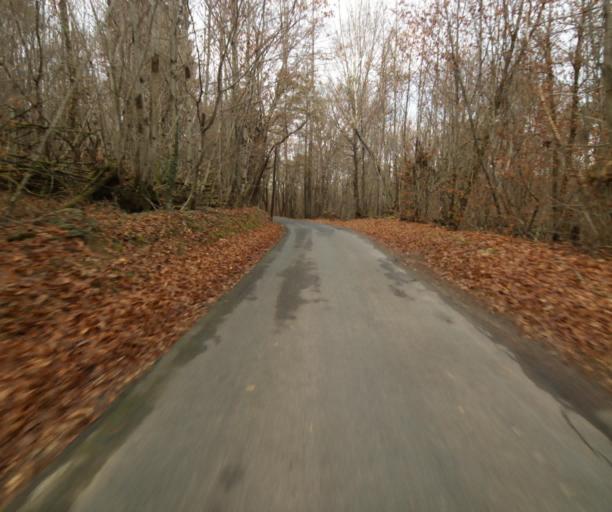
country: FR
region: Limousin
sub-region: Departement de la Correze
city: Laguenne
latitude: 45.2319
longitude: 1.7617
